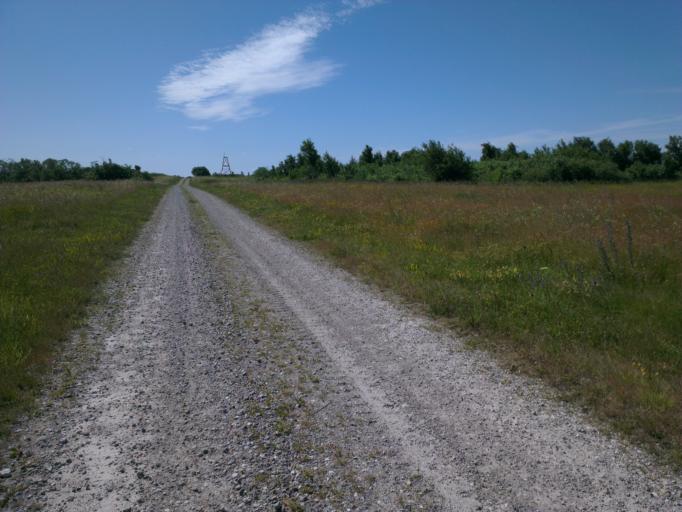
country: DK
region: Capital Region
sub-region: Frederikssund Kommune
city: Jaegerspris
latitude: 55.8801
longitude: 11.9376
